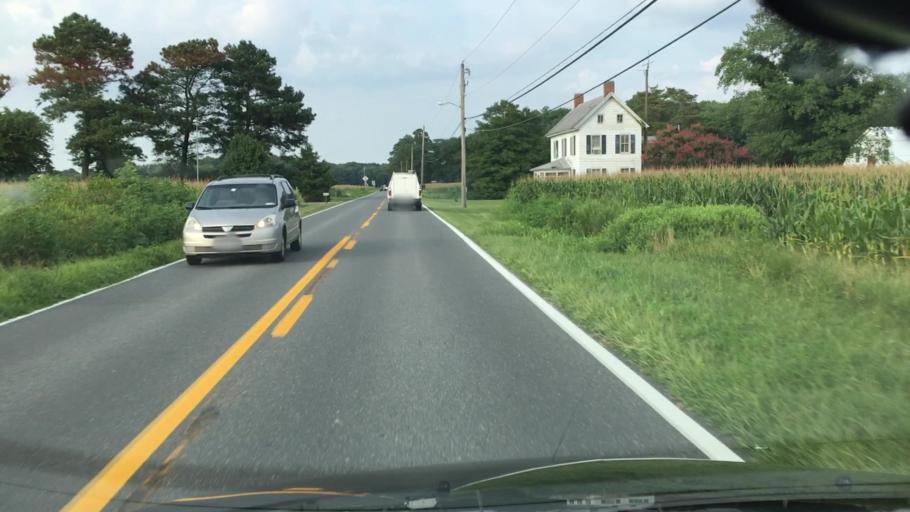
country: US
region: Delaware
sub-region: Sussex County
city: Selbyville
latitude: 38.4487
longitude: -75.1892
